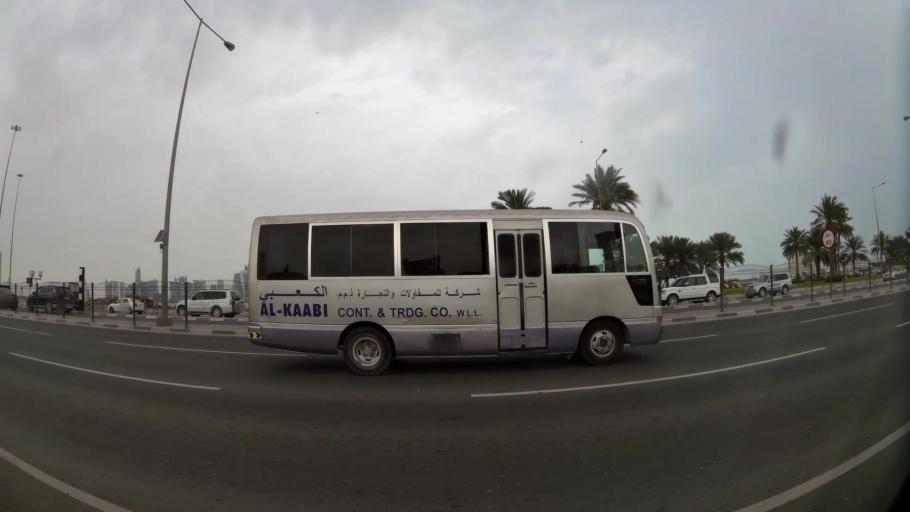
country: QA
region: Baladiyat ad Dawhah
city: Doha
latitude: 25.2916
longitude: 51.5308
